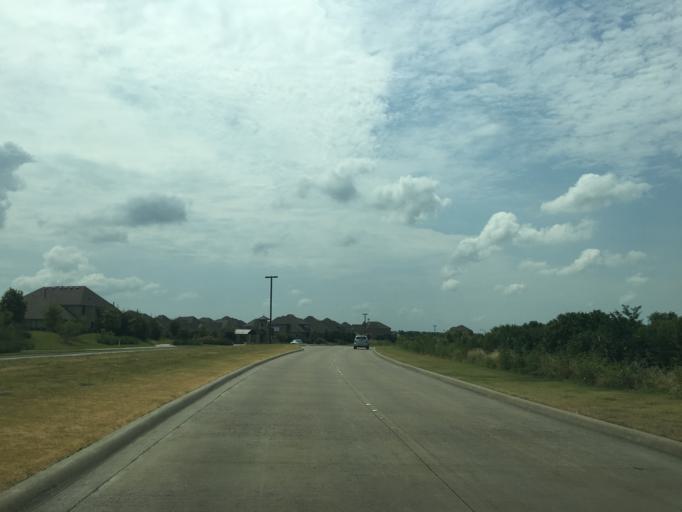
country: US
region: Texas
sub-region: Rockwall County
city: Rockwall
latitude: 32.9725
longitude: -96.4534
